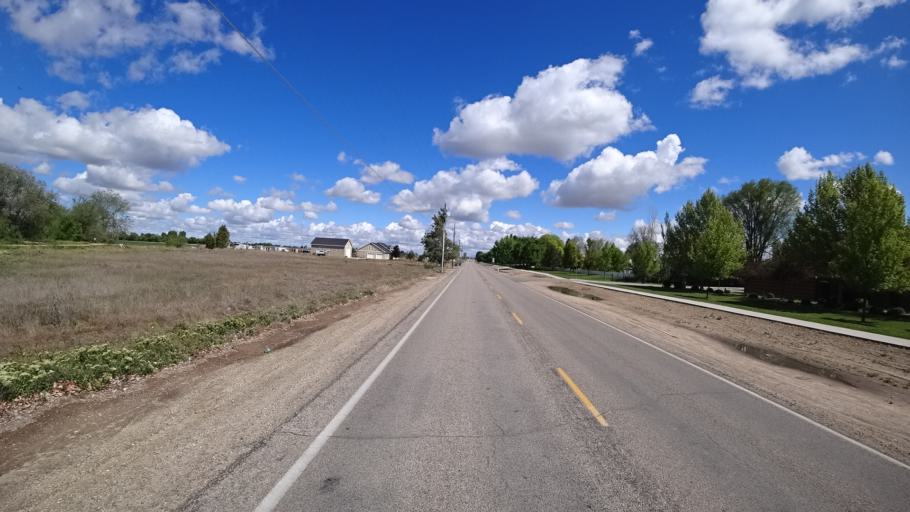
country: US
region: Idaho
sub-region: Ada County
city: Kuna
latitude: 43.4987
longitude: -116.4336
